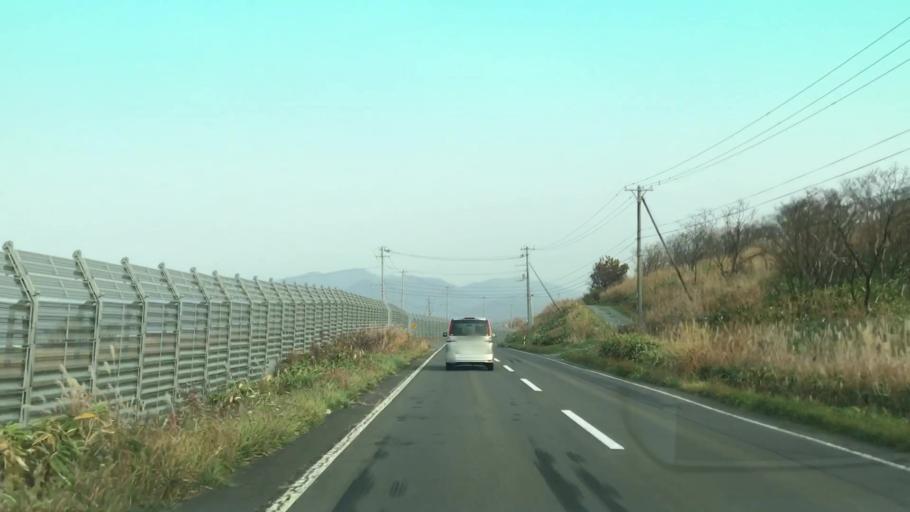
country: JP
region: Hokkaido
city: Ishikari
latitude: 43.3783
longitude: 141.4286
